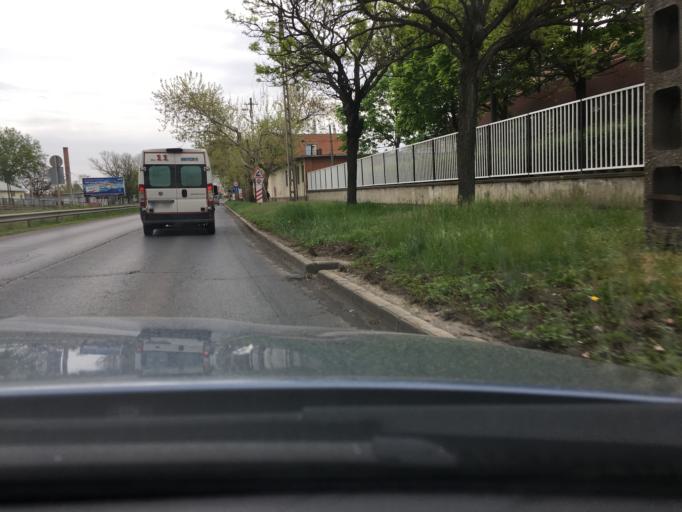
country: HU
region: Hajdu-Bihar
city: Debrecen
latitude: 47.5206
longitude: 21.6556
